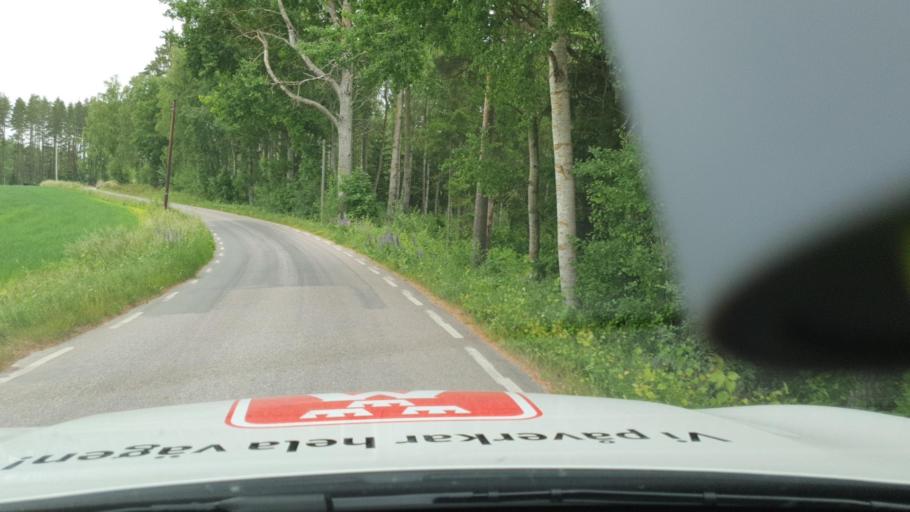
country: SE
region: Vaestra Goetaland
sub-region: Tibro Kommun
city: Tibro
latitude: 58.3519
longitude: 14.1573
